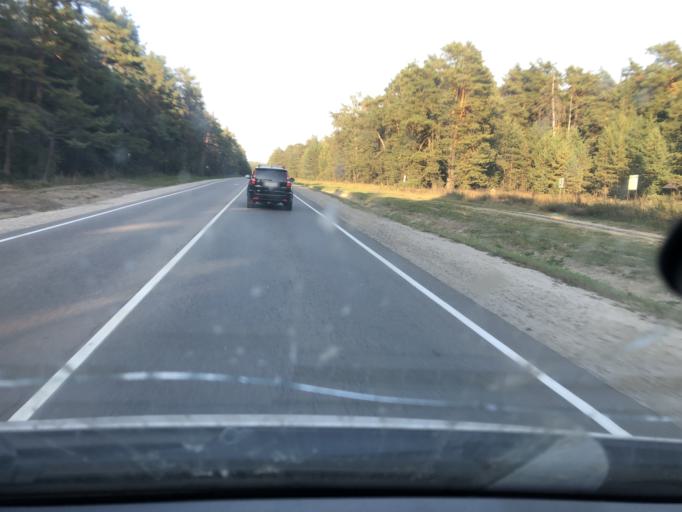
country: RU
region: Kaluga
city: Peremyshl'
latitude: 54.3504
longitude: 36.1931
